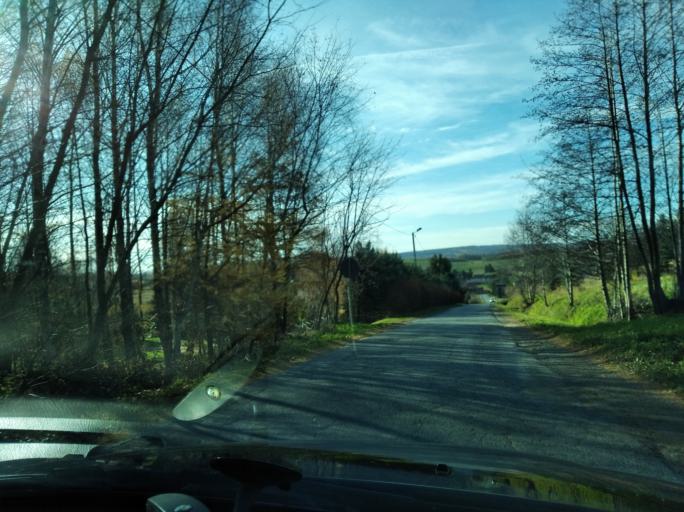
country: PL
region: Subcarpathian Voivodeship
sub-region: Powiat rzeszowski
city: Kielanowka
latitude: 50.0099
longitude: 21.9113
